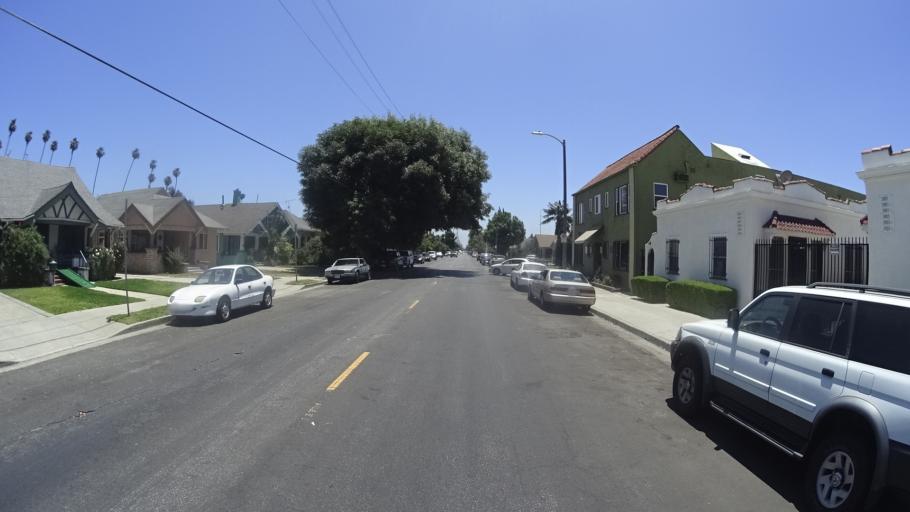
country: US
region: California
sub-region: Los Angeles County
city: View Park-Windsor Hills
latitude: 34.0145
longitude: -118.3046
